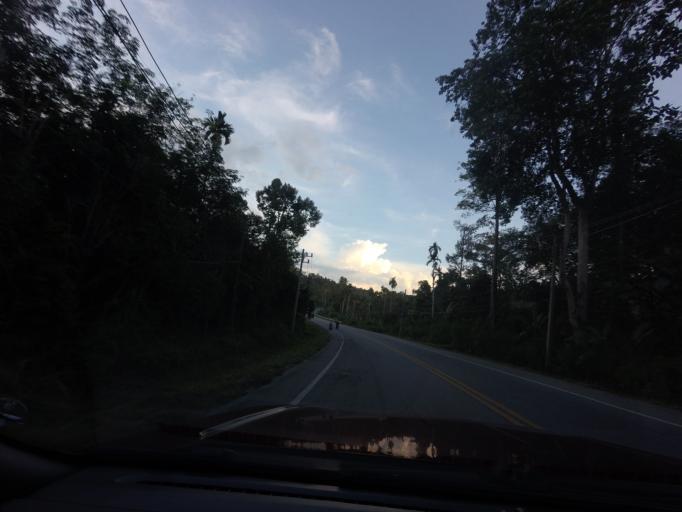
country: TH
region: Yala
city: Than To
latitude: 6.1047
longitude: 101.1823
